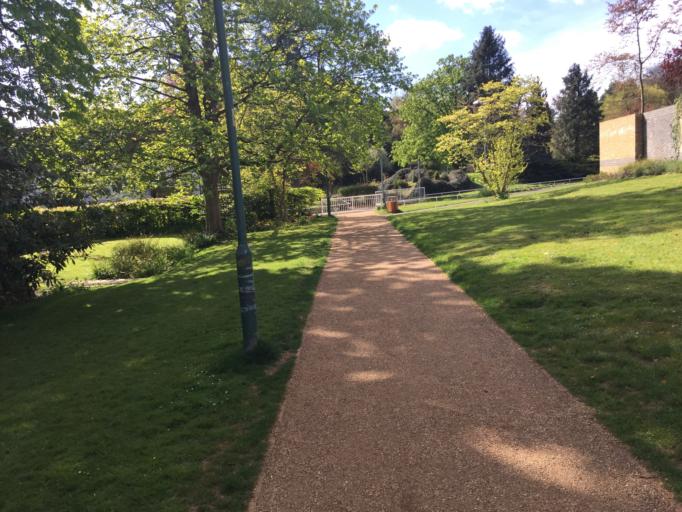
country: GB
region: England
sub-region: Essex
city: Harlow
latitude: 51.7780
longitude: 0.1004
